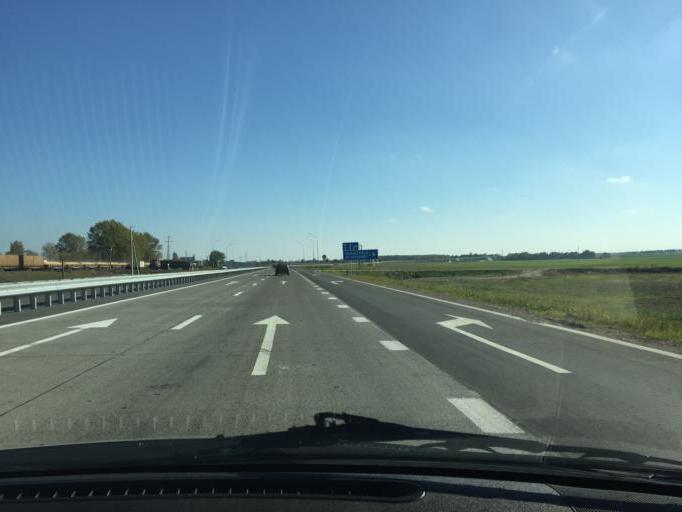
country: BY
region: Minsk
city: Slutsk
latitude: 53.0032
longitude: 27.4944
